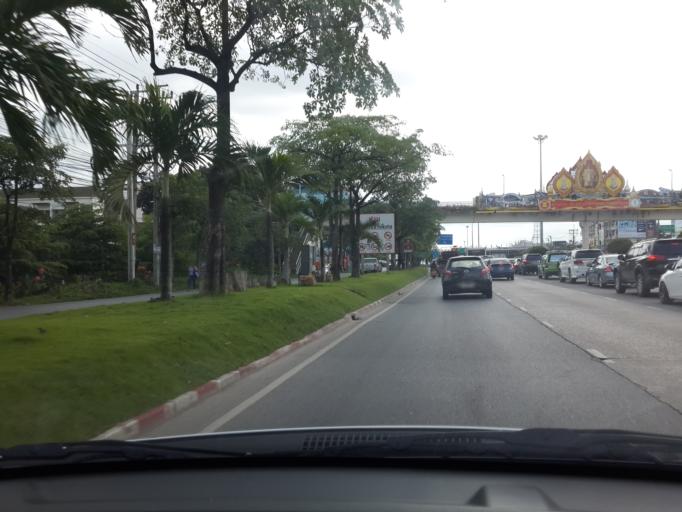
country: TH
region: Bangkok
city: Saphan Sung
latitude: 13.7851
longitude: 100.6886
